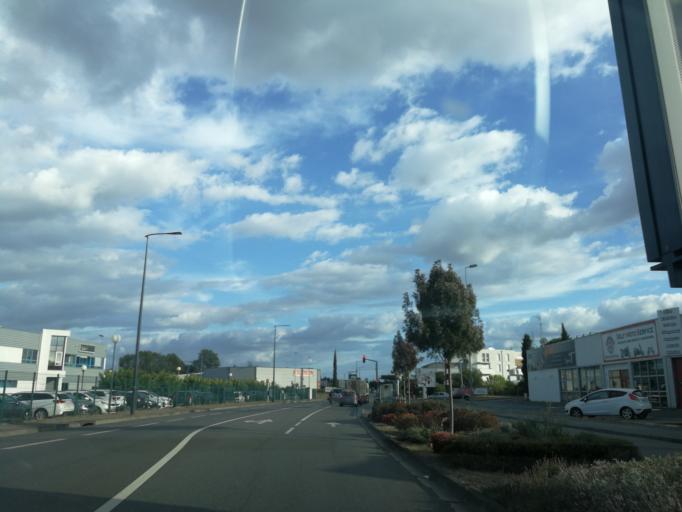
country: FR
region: Midi-Pyrenees
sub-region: Departement de la Haute-Garonne
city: L'Union
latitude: 43.6408
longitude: 1.4689
